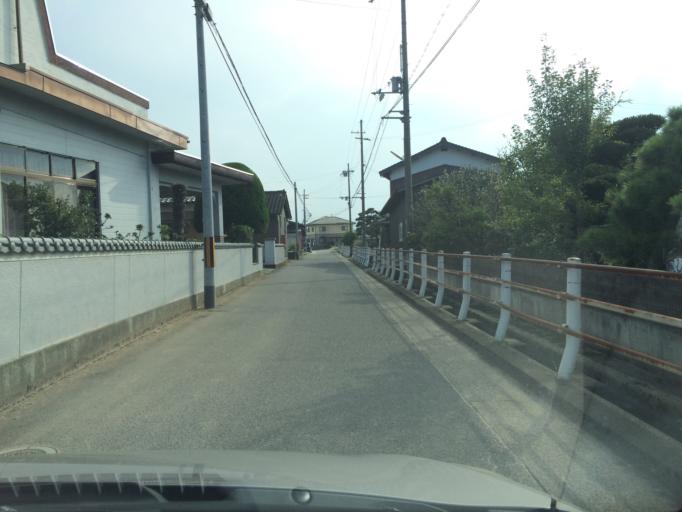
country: JP
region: Hyogo
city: Toyooka
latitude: 35.5221
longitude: 134.8272
